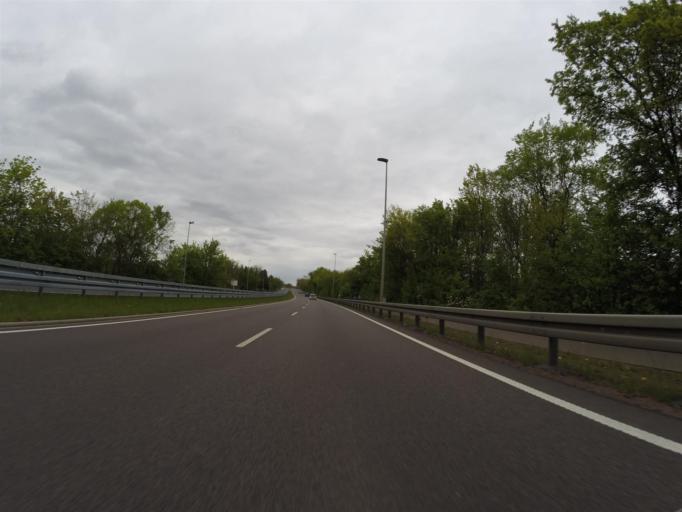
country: DE
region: Saxony-Anhalt
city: Schkopau
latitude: 51.3790
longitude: 11.9820
